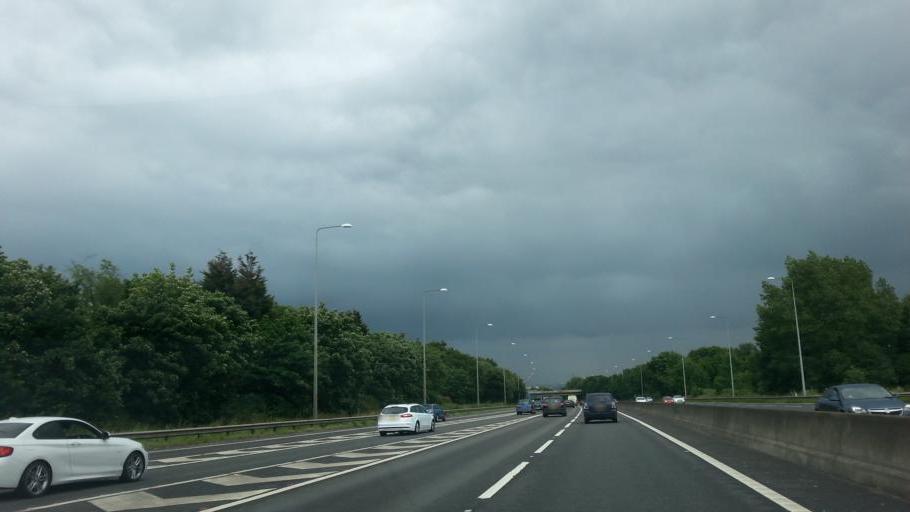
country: GB
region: England
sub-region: City and Borough of Leeds
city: Lofthouse
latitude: 53.7292
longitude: -1.5037
